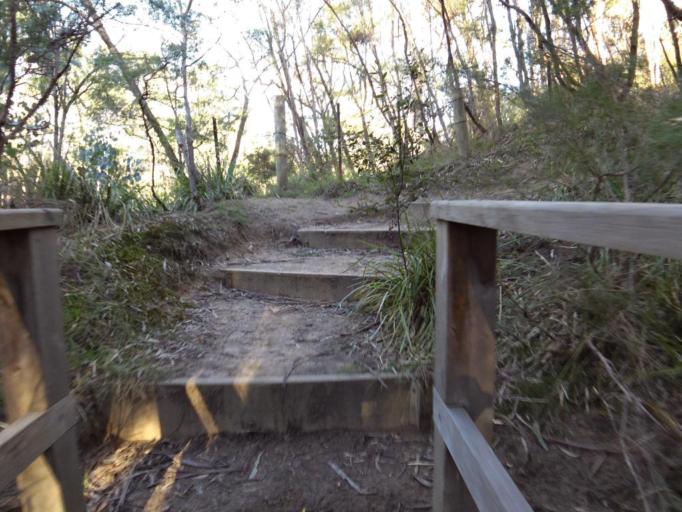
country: AU
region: Victoria
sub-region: Manningham
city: Warrandyte
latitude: -37.7326
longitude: 145.2371
